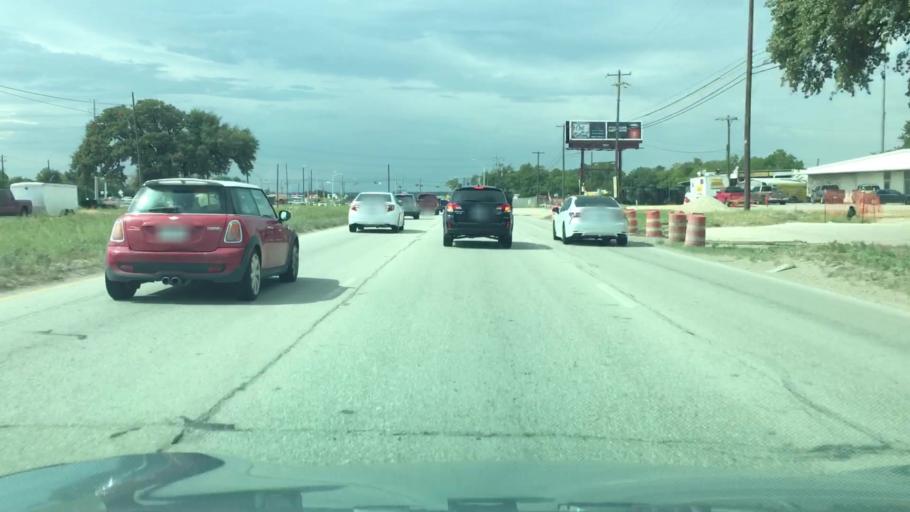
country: US
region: Texas
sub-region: Travis County
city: Austin
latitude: 30.2382
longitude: -97.6868
